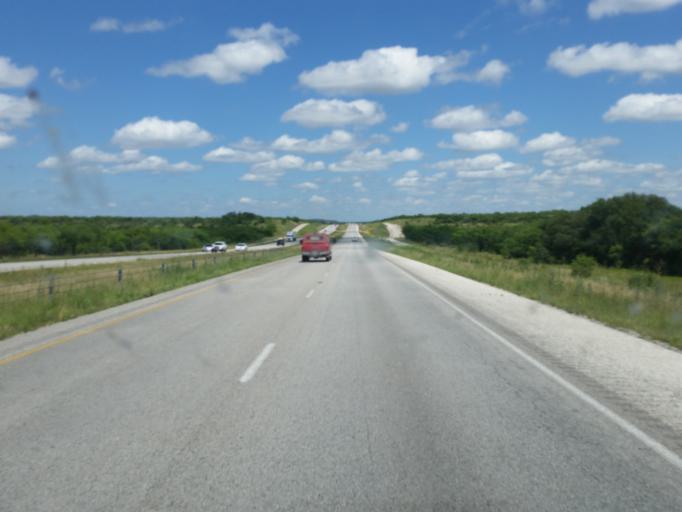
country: US
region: Texas
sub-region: Callahan County
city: Baird
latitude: 32.3822
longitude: -99.2770
